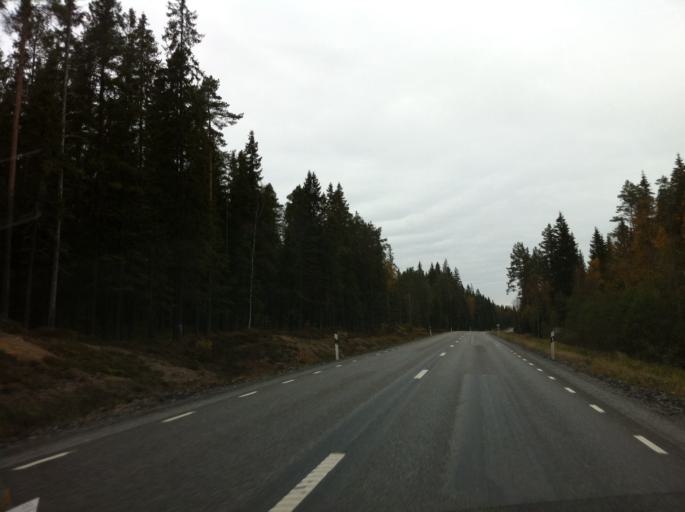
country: SE
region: OErebro
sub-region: Ljusnarsbergs Kommun
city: Kopparberg
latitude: 59.9165
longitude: 15.0223
